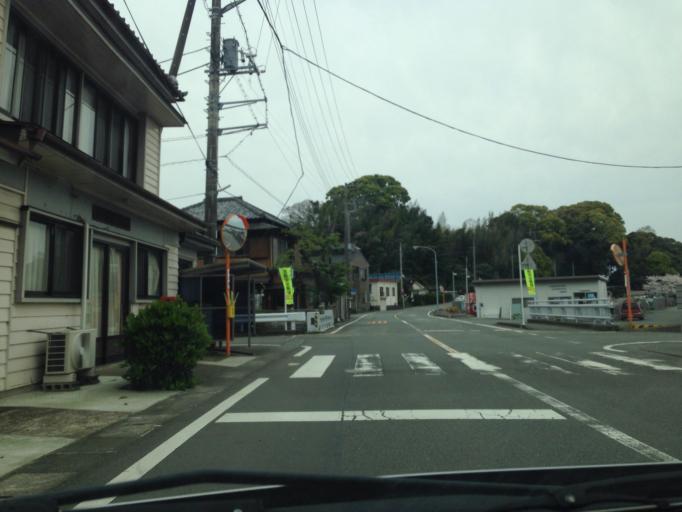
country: JP
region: Shizuoka
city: Heda
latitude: 35.0177
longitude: 138.8379
